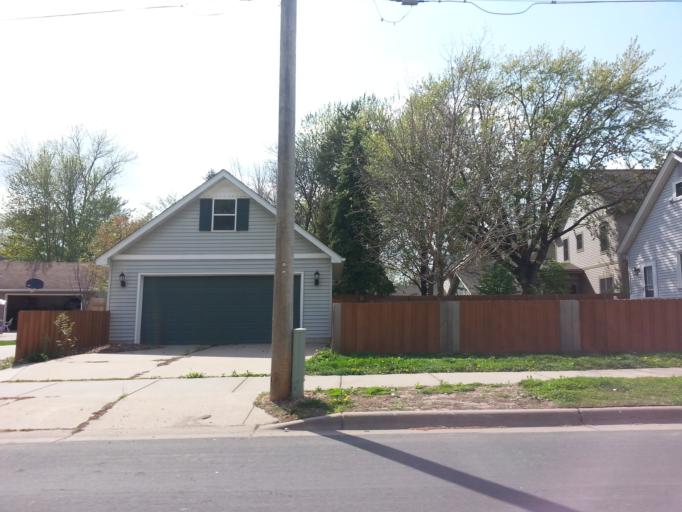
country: US
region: Minnesota
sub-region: Washington County
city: Stillwater
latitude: 45.0476
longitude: -92.8128
